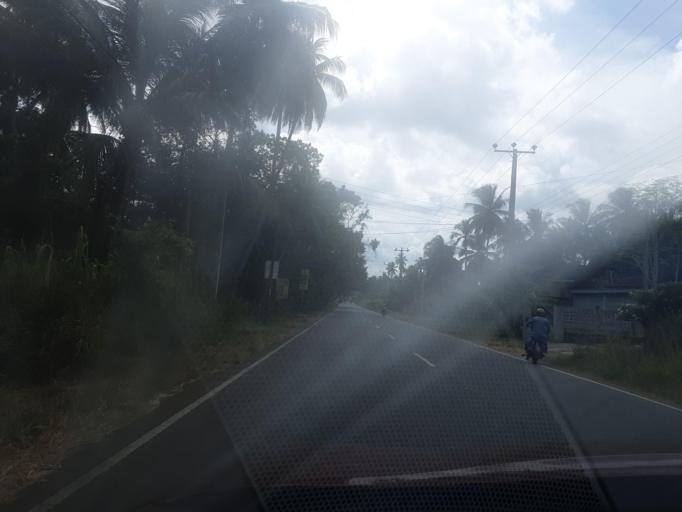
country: LK
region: North Western
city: Kuliyapitiya
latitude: 7.4797
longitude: 79.9991
